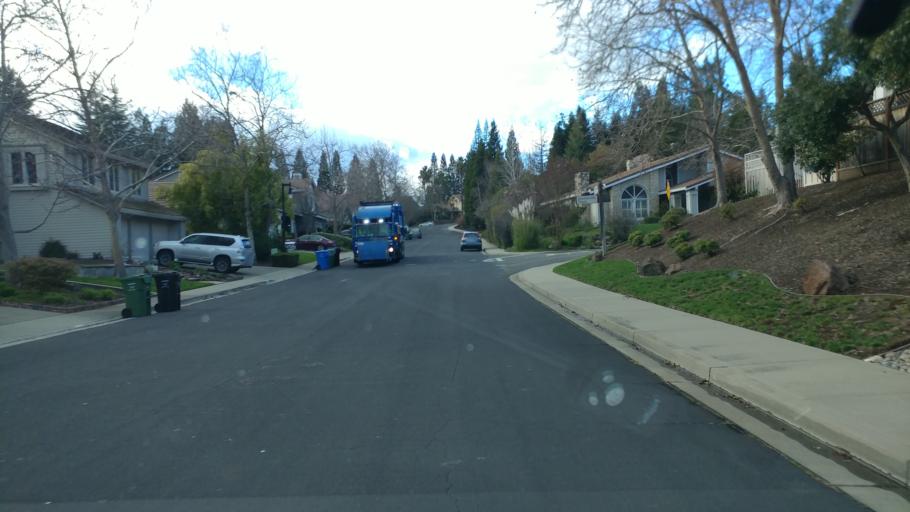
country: US
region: California
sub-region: Contra Costa County
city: Diablo
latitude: 37.8189
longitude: -121.9719
